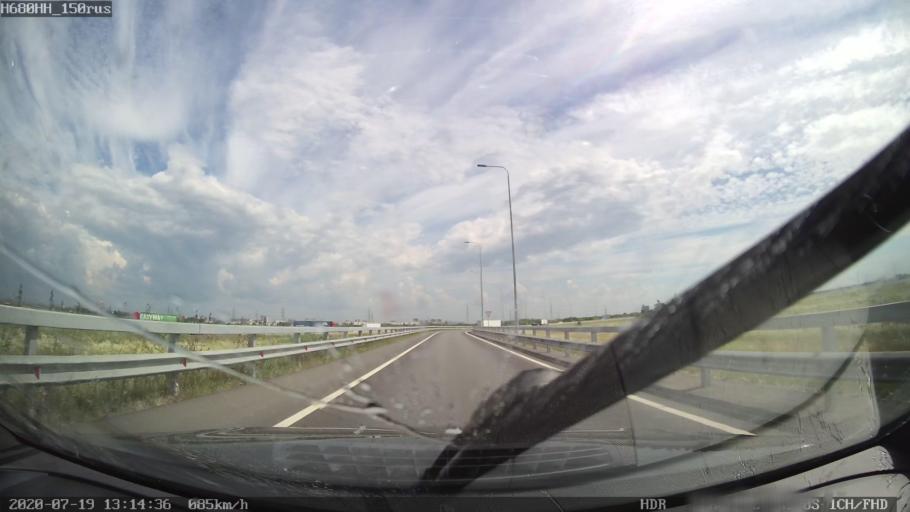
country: RU
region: St.-Petersburg
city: Kolpino
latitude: 59.7308
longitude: 30.5269
